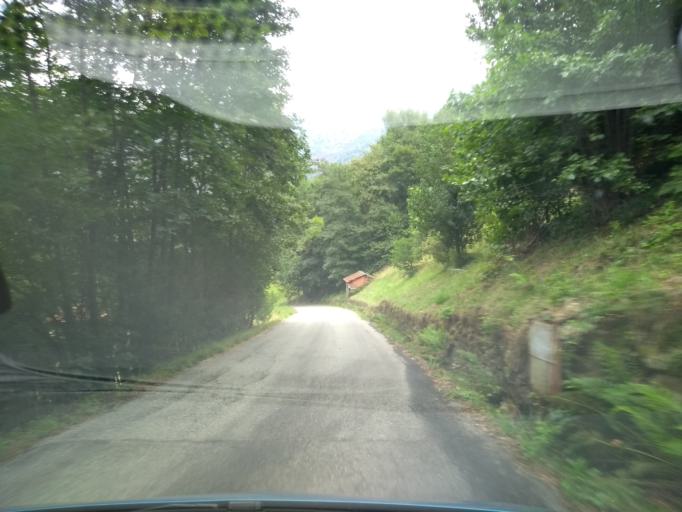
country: IT
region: Piedmont
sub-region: Provincia di Torino
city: La Villa
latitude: 45.2348
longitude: 7.4297
